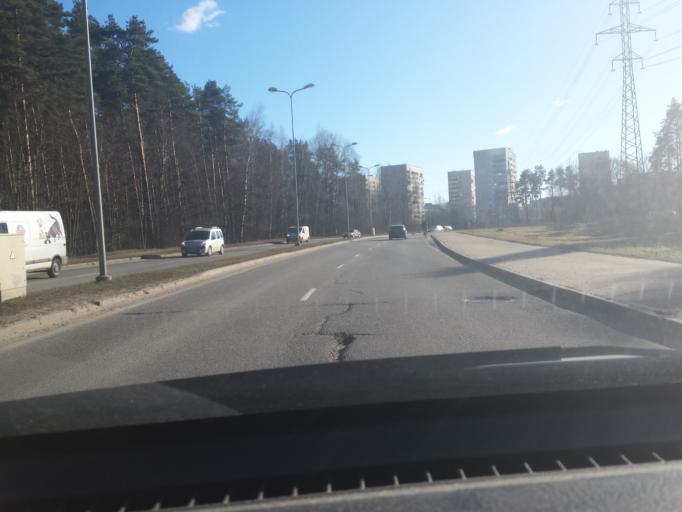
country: LV
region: Riga
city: Jaunciems
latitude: 56.9636
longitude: 24.1999
